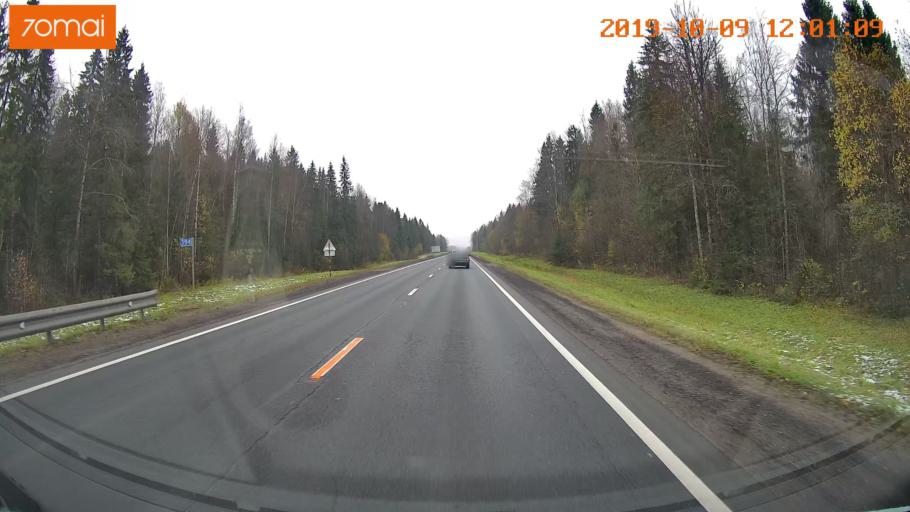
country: RU
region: Vologda
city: Gryazovets
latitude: 58.6914
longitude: 40.3020
